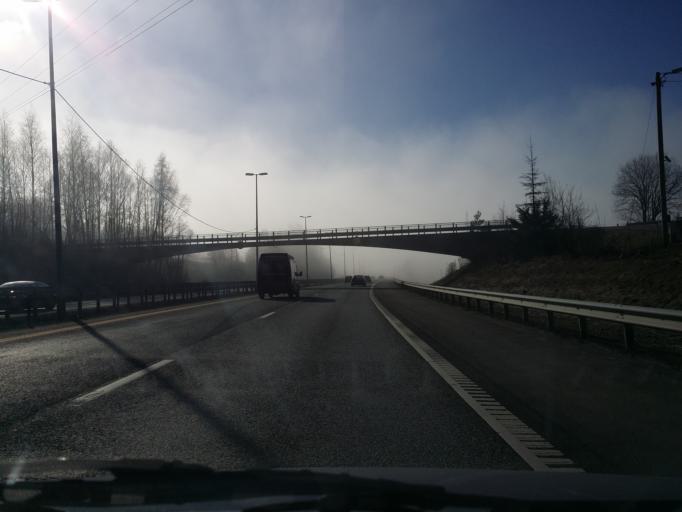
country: NO
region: Buskerud
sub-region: Lier
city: Tranby
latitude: 59.7887
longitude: 10.2727
